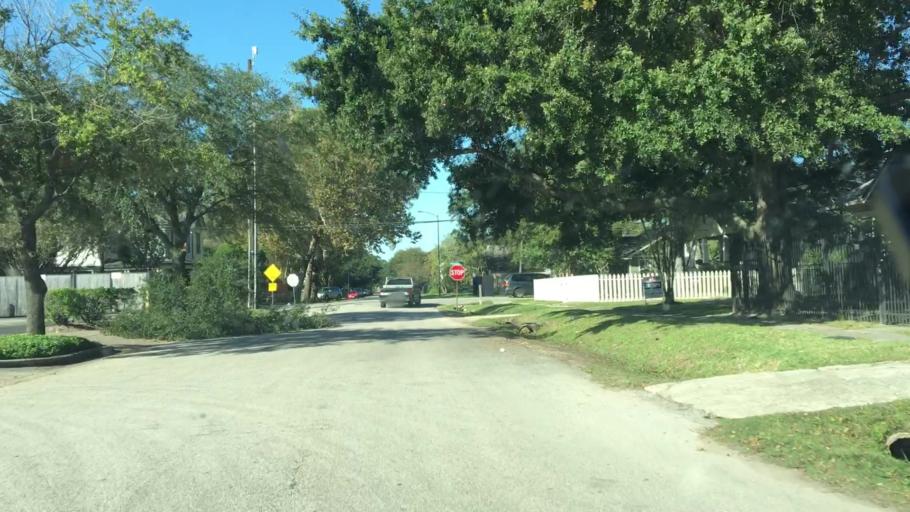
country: US
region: Texas
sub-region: Harris County
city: Houston
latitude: 29.8050
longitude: -95.4009
